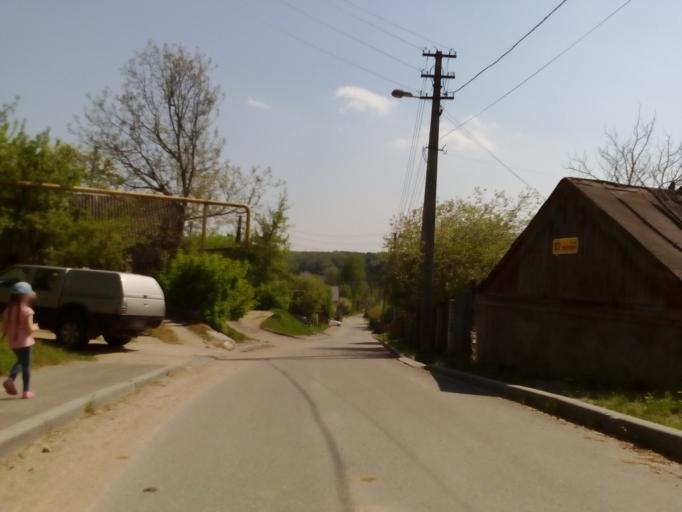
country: BY
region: Grodnenskaya
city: Hrodna
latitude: 53.6656
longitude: 23.8500
